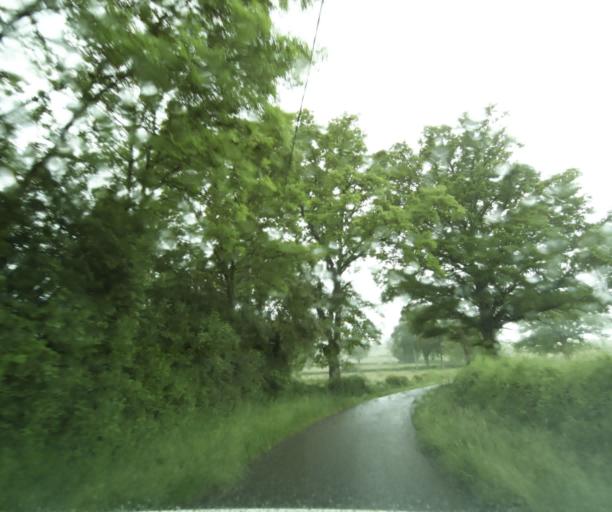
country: FR
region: Bourgogne
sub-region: Departement de Saone-et-Loire
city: Ciry-le-Noble
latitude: 46.5342
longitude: 4.3669
